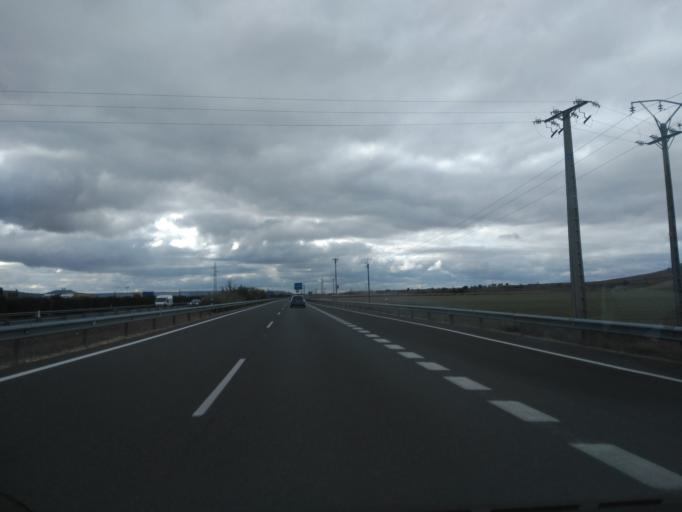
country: ES
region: Castille and Leon
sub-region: Provincia de Palencia
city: Duenas
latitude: 41.8480
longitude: -4.5595
